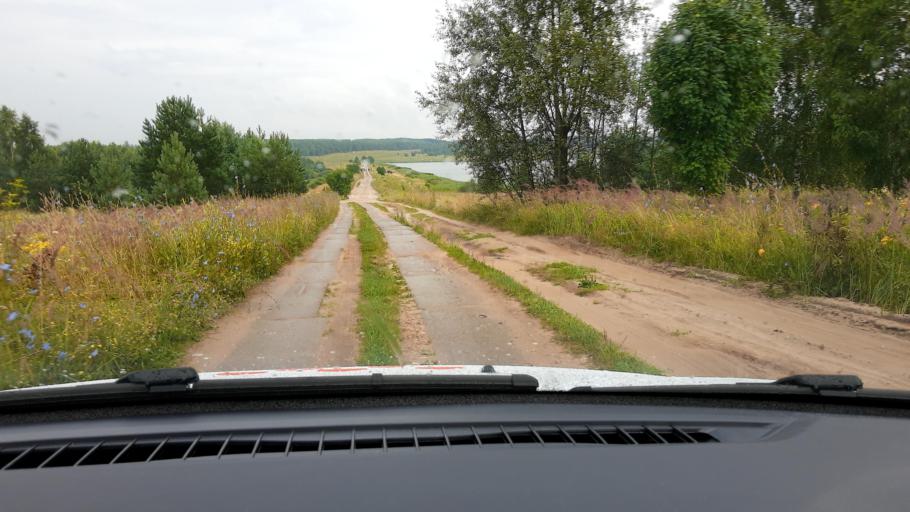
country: RU
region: Nizjnij Novgorod
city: Surovatikha
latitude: 55.9412
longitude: 43.9164
